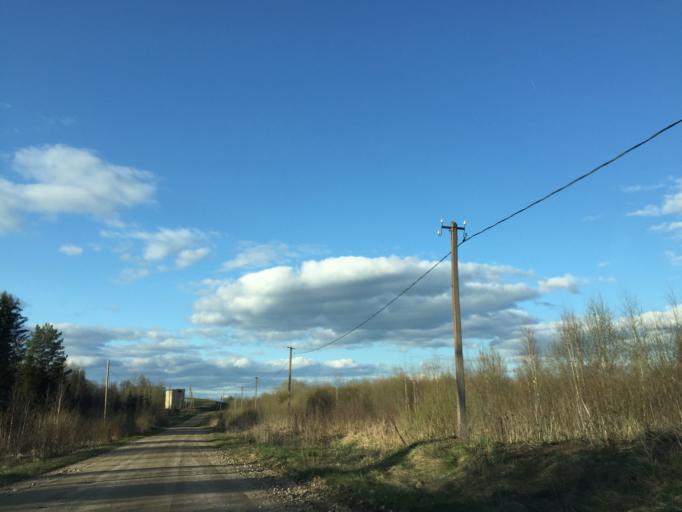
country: LV
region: Rezekne
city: Rezekne
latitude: 56.5837
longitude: 27.3379
